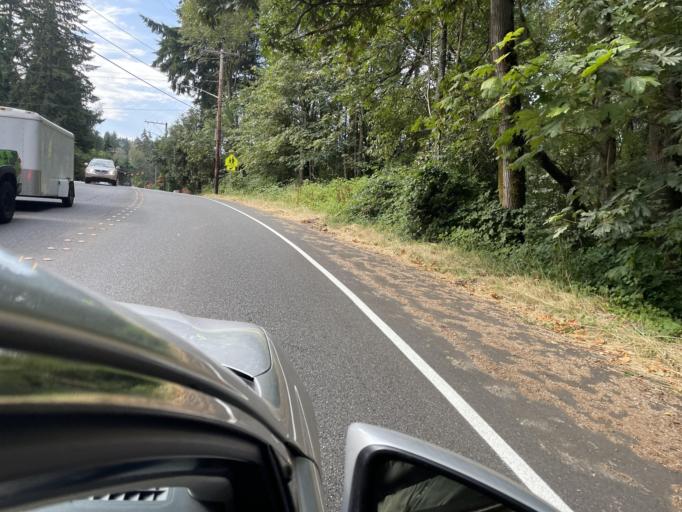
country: US
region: Washington
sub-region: King County
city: Eastgate
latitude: 47.5664
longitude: -122.1428
